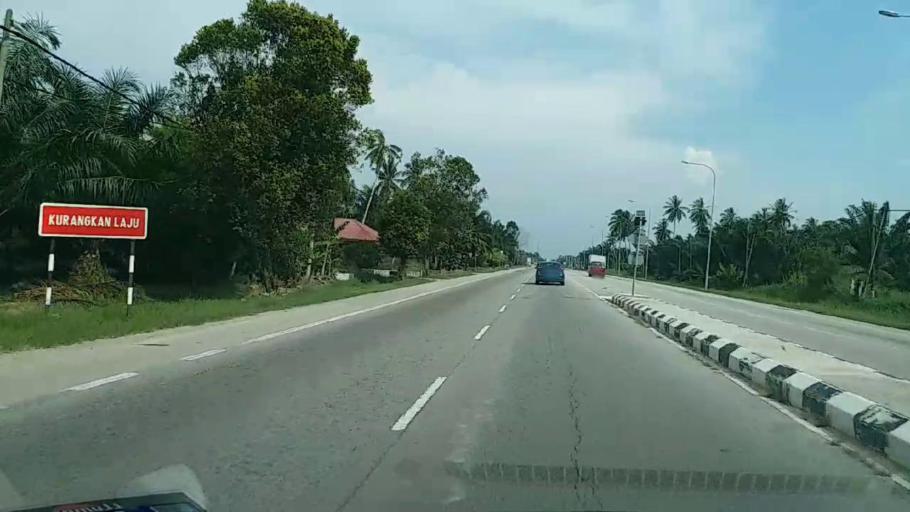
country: MY
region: Selangor
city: Kuala Selangor
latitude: 3.3764
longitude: 101.2367
